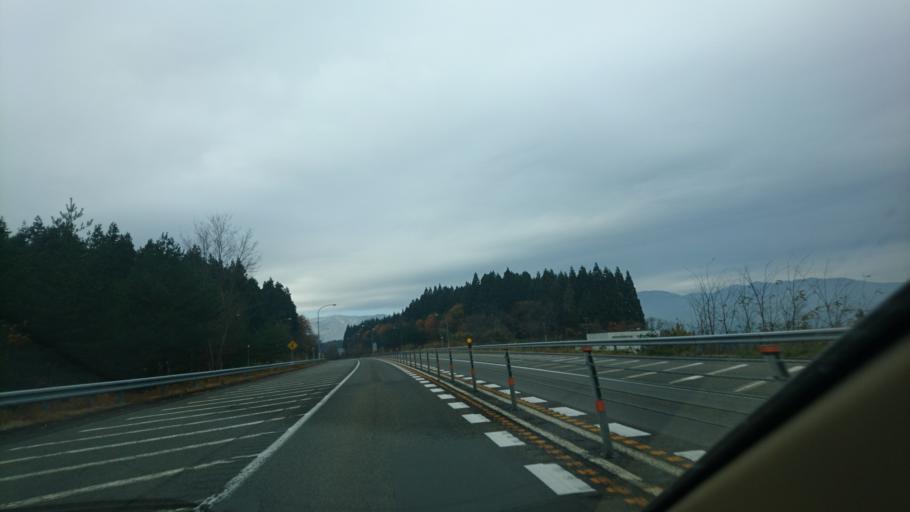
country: JP
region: Iwate
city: Kitakami
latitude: 39.2918
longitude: 140.9844
